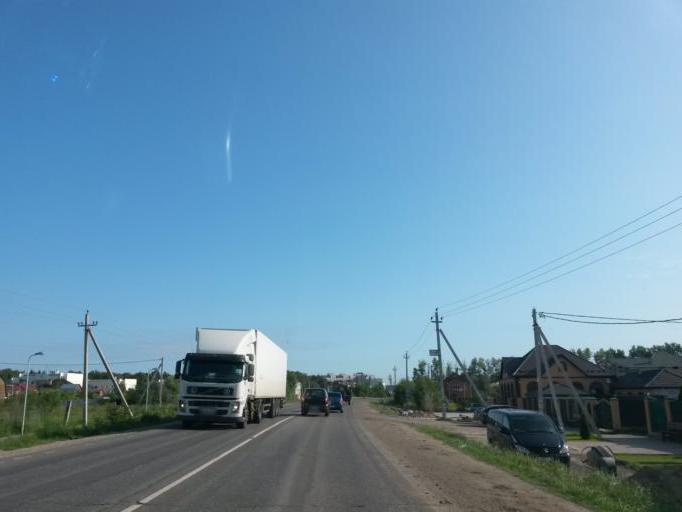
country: RU
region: Moskovskaya
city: Gorki-Leninskiye
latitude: 55.5022
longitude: 37.7803
